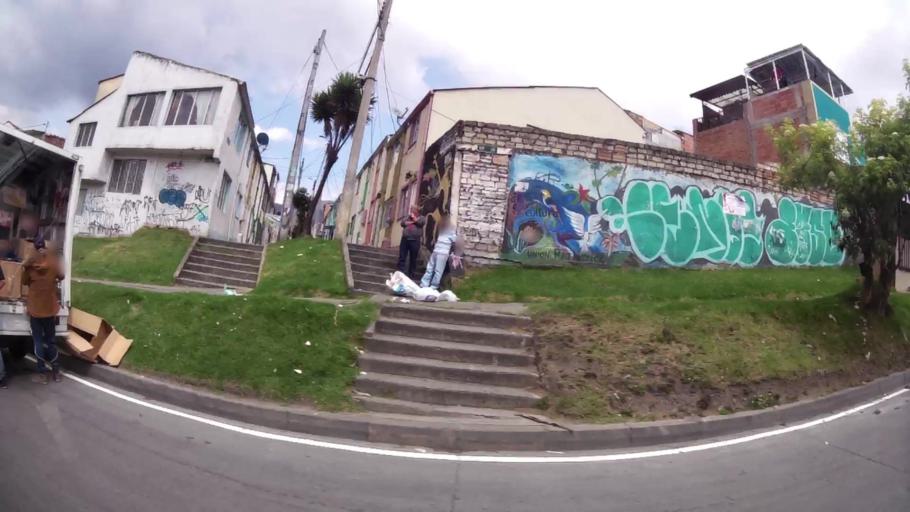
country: CO
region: Bogota D.C.
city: Bogota
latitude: 4.5613
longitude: -74.0982
